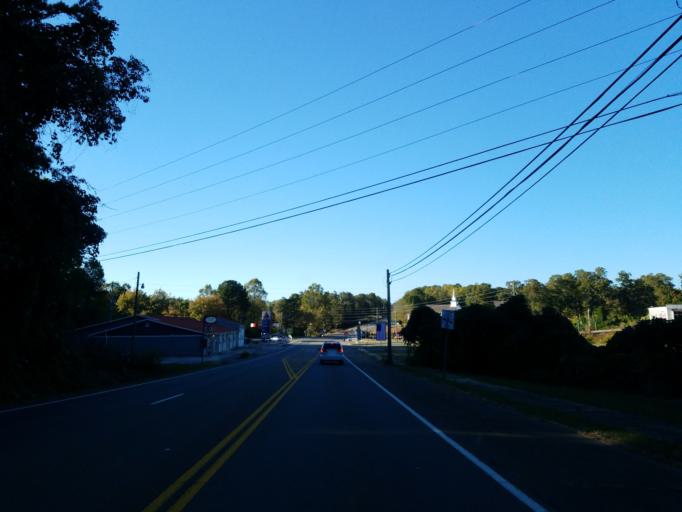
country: US
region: Georgia
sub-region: Pickens County
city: Nelson
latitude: 34.4119
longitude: -84.3879
